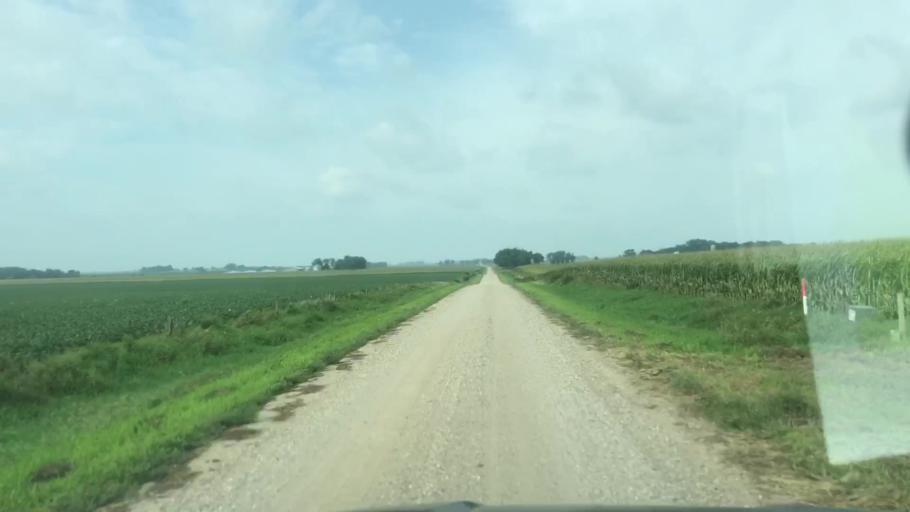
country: US
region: Iowa
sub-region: O'Brien County
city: Sheldon
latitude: 43.2723
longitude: -95.8838
